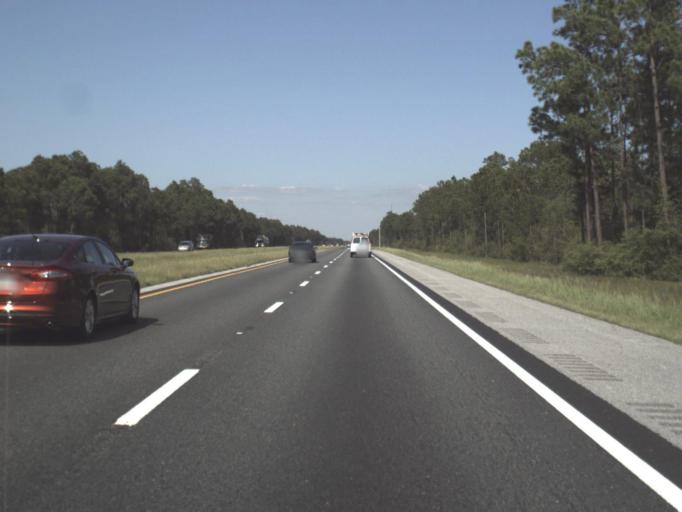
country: US
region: Florida
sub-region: Santa Rosa County
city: Bagdad
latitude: 30.5452
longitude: -87.0632
